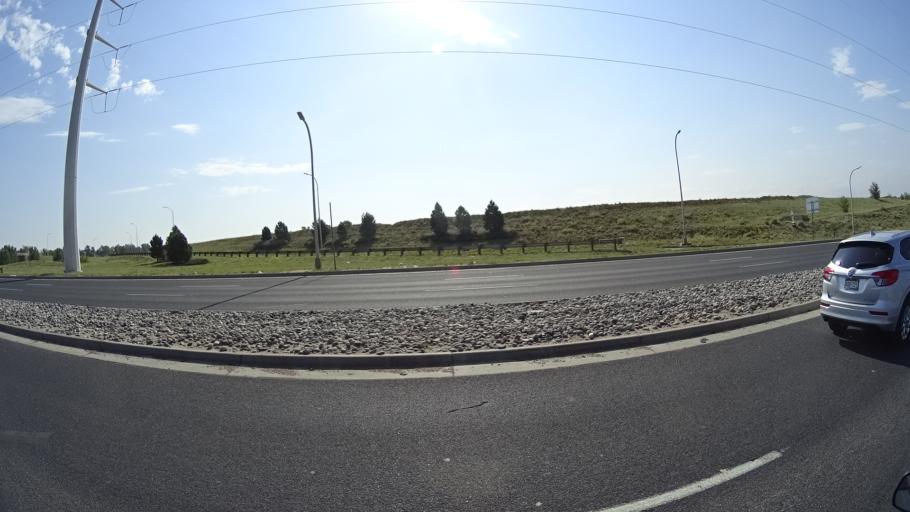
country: US
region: Colorado
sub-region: El Paso County
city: Stratmoor
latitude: 38.7792
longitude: -104.7571
